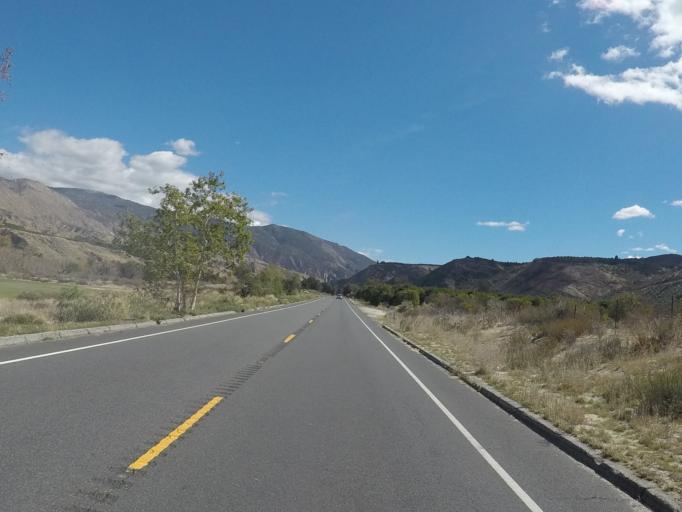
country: US
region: California
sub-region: Riverside County
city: Valle Vista
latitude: 33.7403
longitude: -116.8455
